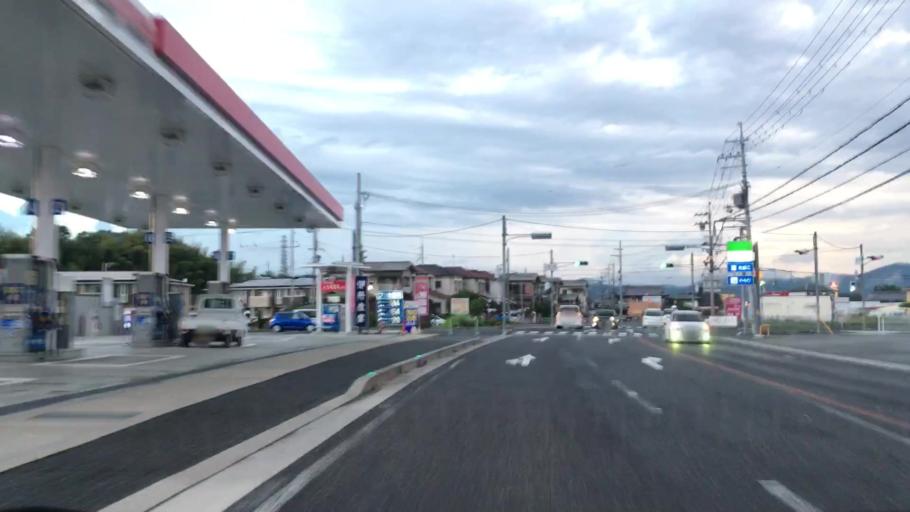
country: JP
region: Hyogo
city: Himeji
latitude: 34.9241
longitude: 134.7441
